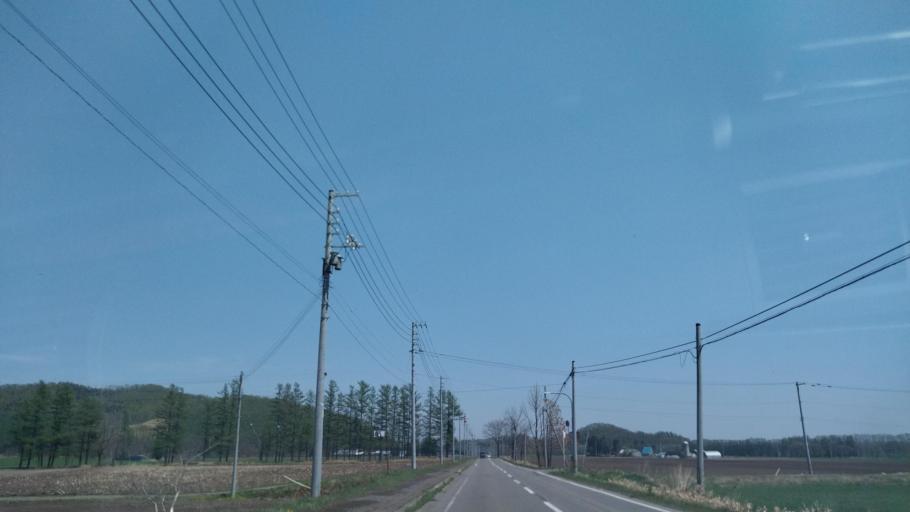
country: JP
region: Hokkaido
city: Obihiro
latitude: 42.8148
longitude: 142.9736
